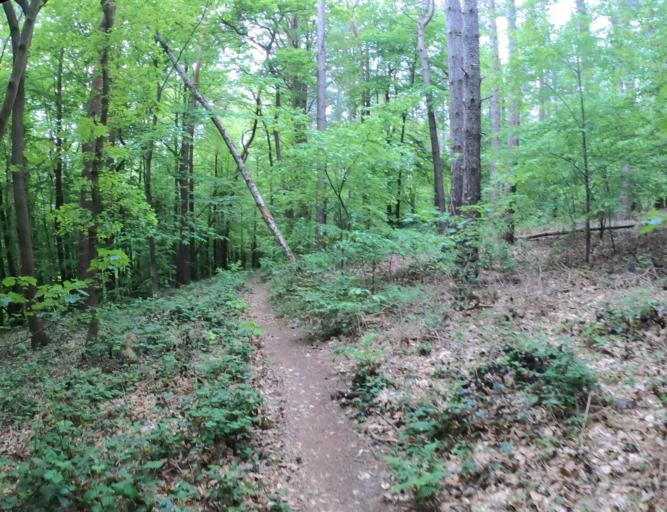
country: BE
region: Flanders
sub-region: Provincie Vlaams-Brabant
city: Beersel
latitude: 50.7383
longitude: 4.3080
